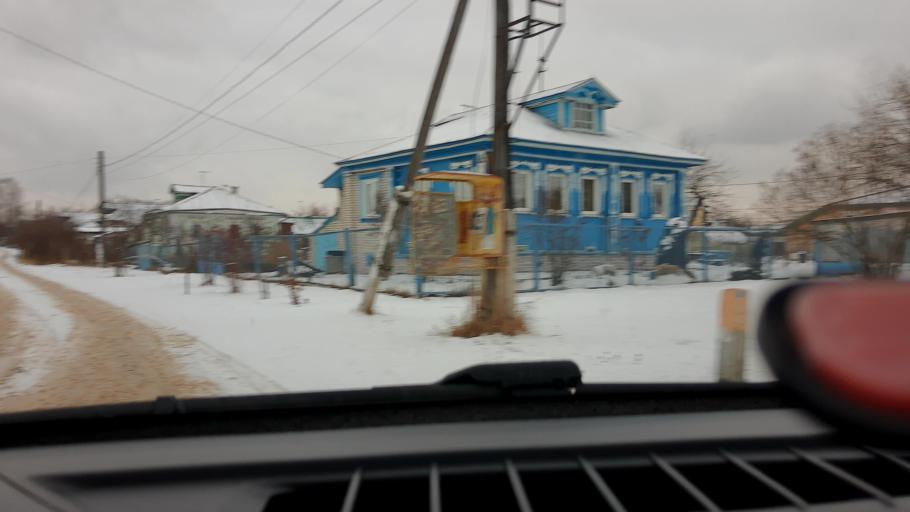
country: RU
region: Nizjnij Novgorod
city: Gorbatovka
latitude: 56.2685
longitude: 43.7677
